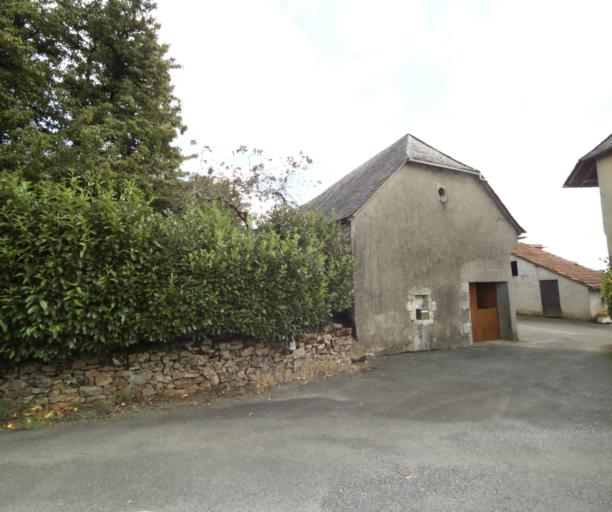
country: FR
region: Limousin
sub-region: Departement de la Correze
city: Sainte-Fortunade
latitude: 45.1945
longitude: 1.8264
